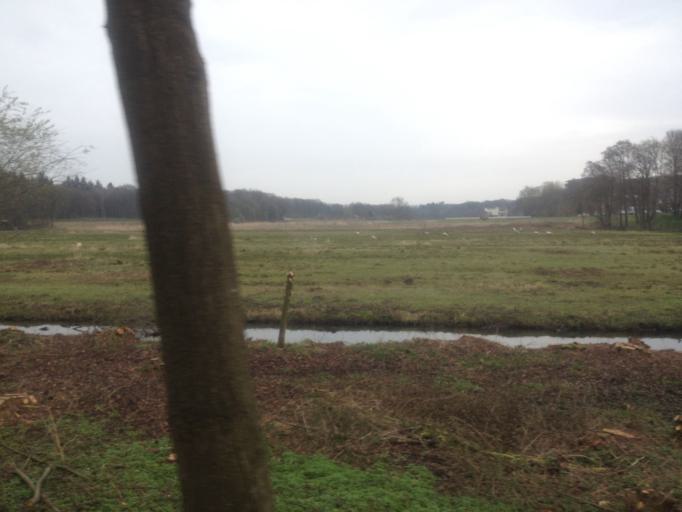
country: NL
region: Gelderland
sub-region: Gemeente Renkum
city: Renkum
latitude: 51.9744
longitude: 5.7203
